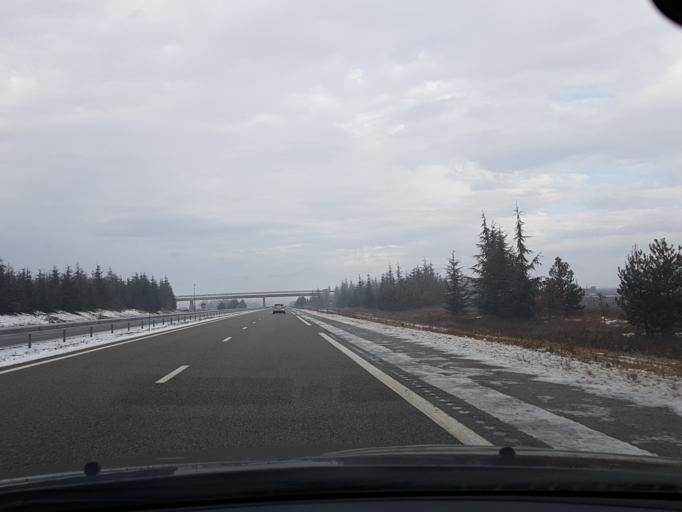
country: FR
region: Provence-Alpes-Cote d'Azur
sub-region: Departement des Alpes-de-Haute-Provence
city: Sisteron
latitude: 44.2369
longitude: 5.9154
